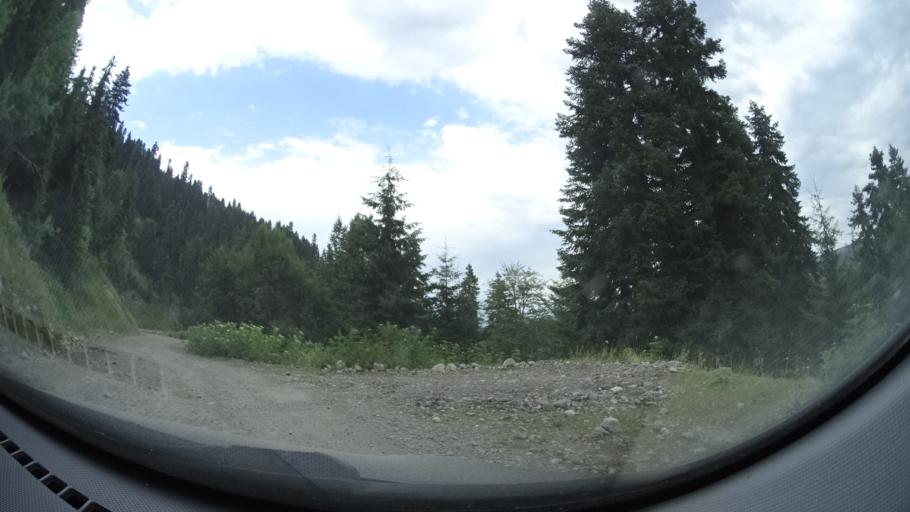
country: GE
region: Samtskhe-Javakheti
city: Adigeni
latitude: 41.6358
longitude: 42.5793
